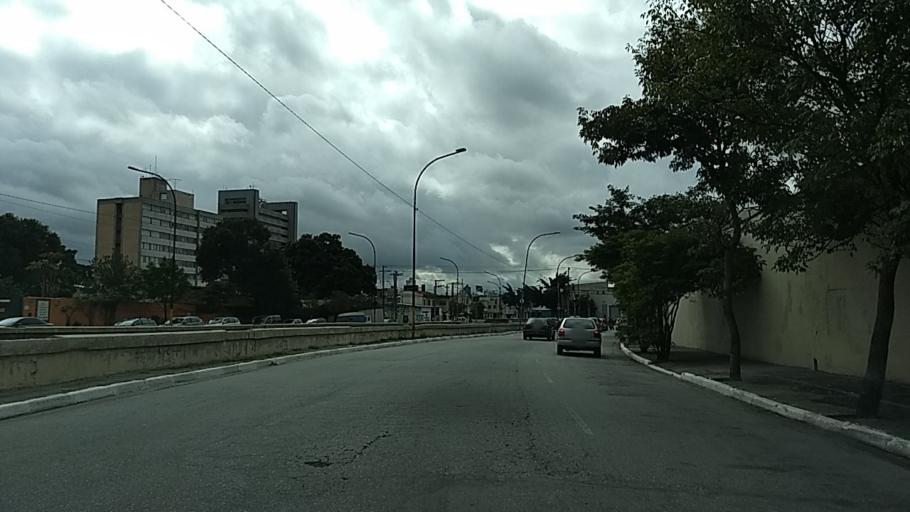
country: BR
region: Sao Paulo
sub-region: Sao Paulo
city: Sao Paulo
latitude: -23.5217
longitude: -46.5959
